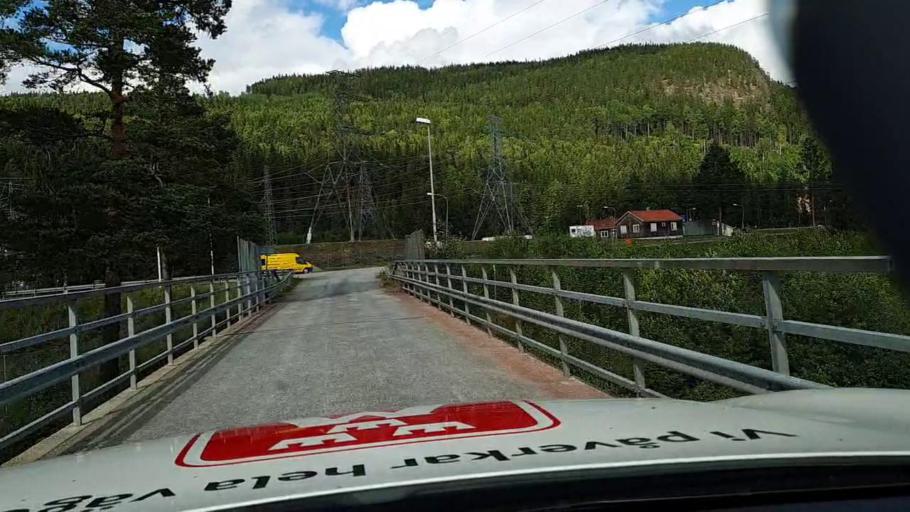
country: SE
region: Jaemtland
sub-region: Ragunda Kommun
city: Hammarstrand
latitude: 63.1461
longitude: 16.0742
